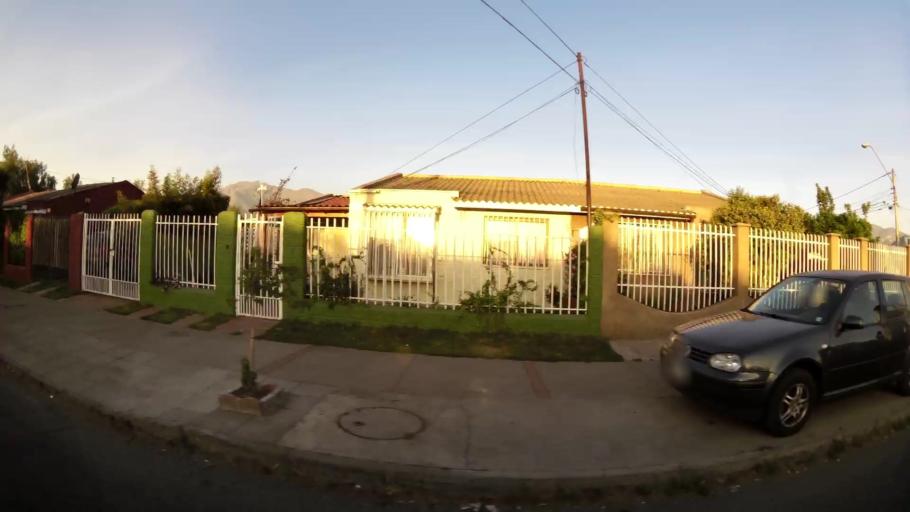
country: CL
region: Santiago Metropolitan
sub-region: Provincia de Cordillera
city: Puente Alto
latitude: -33.5980
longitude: -70.5723
